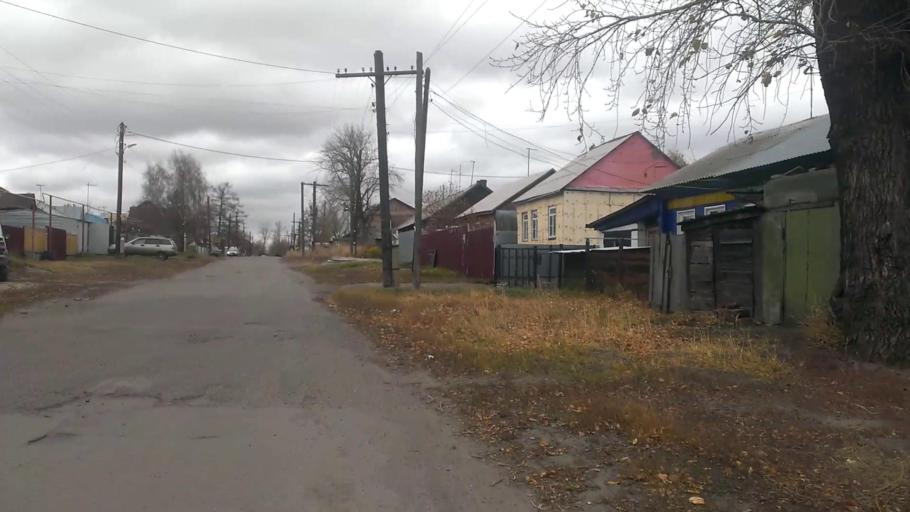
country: RU
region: Altai Krai
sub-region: Gorod Barnaulskiy
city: Barnaul
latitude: 53.3511
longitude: 83.7519
